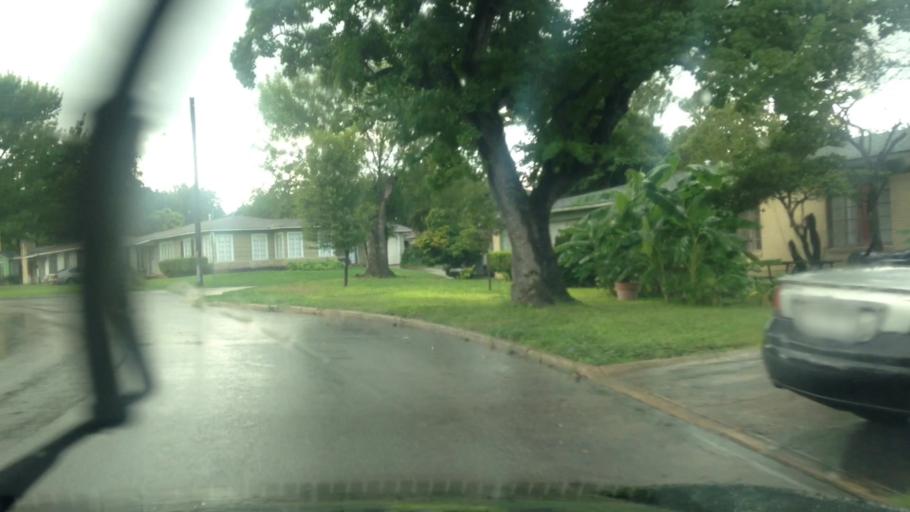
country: US
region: Texas
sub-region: Bexar County
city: Balcones Heights
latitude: 29.4801
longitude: -98.5454
